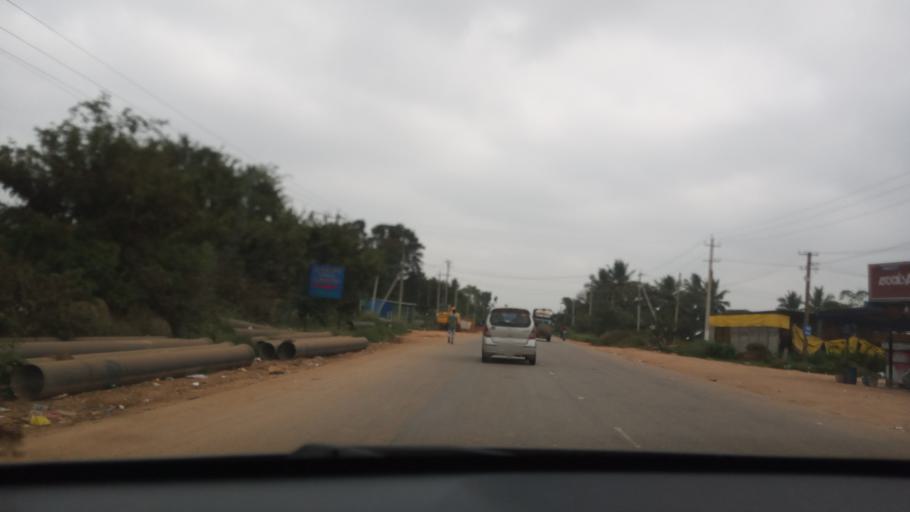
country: IN
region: Karnataka
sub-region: Bangalore Rural
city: Vijayapura
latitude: 13.2612
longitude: 77.9436
